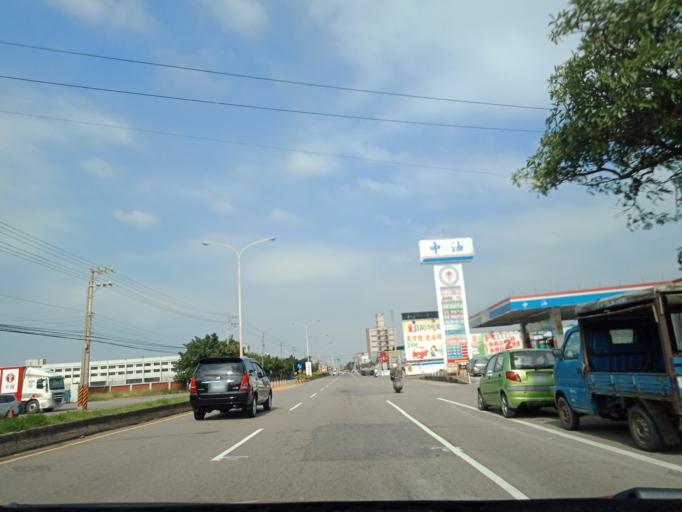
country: TW
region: Taiwan
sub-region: Hsinchu
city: Zhubei
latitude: 24.8826
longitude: 121.0109
